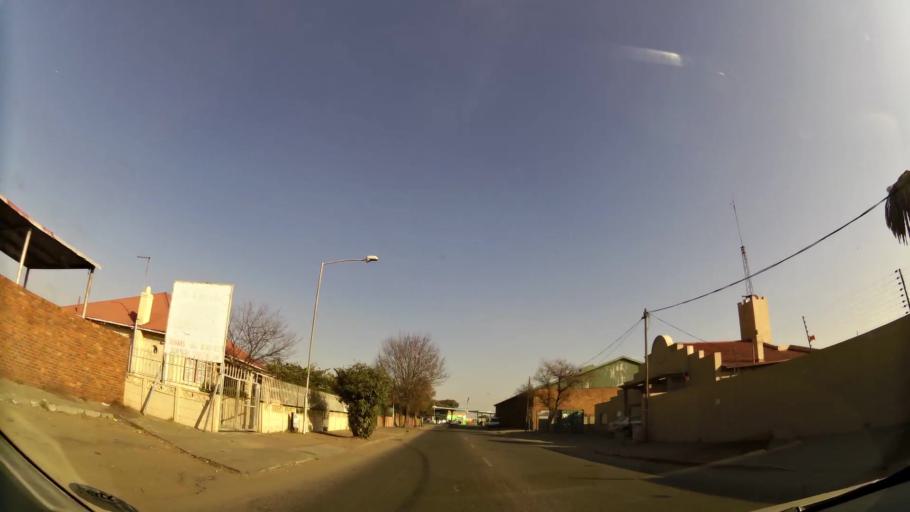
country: ZA
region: Gauteng
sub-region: West Rand District Municipality
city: Randfontein
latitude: -26.1834
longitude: 27.6987
